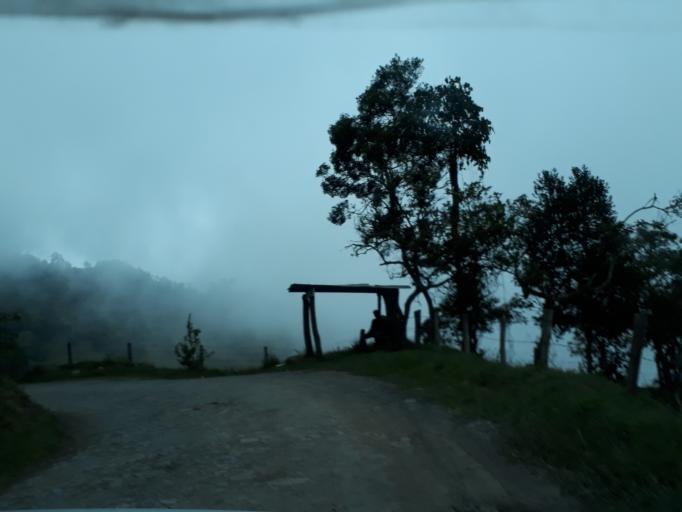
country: CO
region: Boyaca
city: Muzo
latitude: 5.3720
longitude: -74.0739
